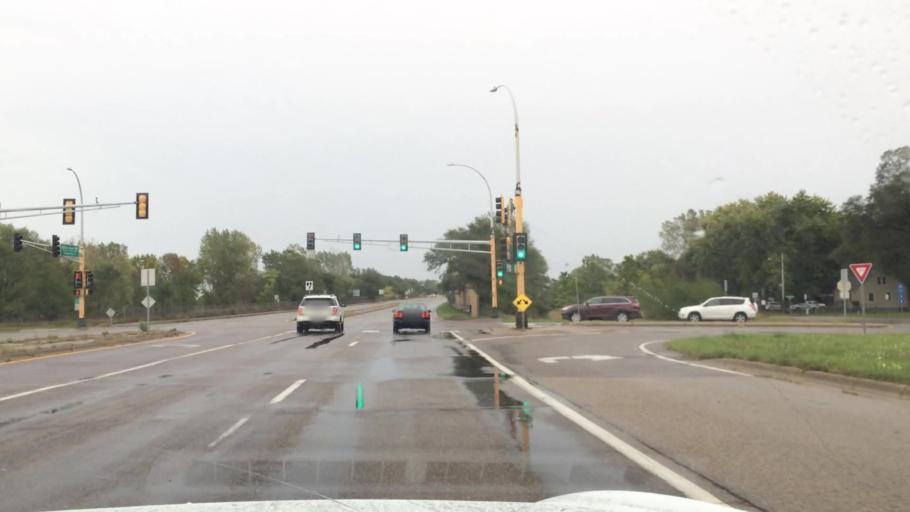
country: US
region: Minnesota
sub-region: Ramsey County
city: Mounds View
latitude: 45.1248
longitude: -93.2189
